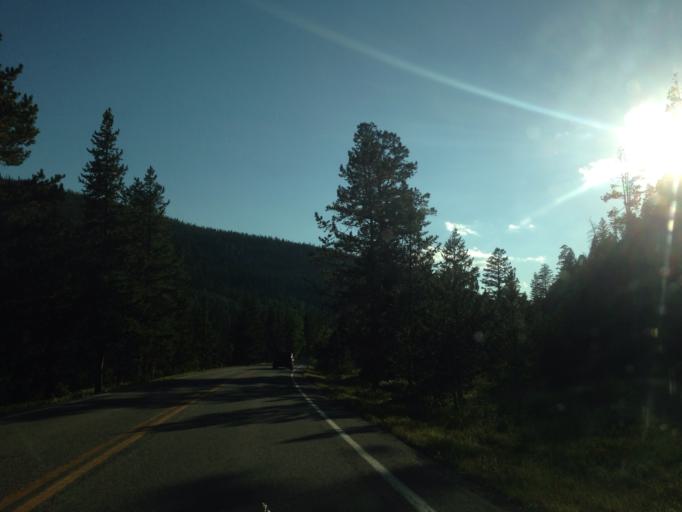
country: US
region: Utah
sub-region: Summit County
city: Francis
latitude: 40.5948
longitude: -110.9761
